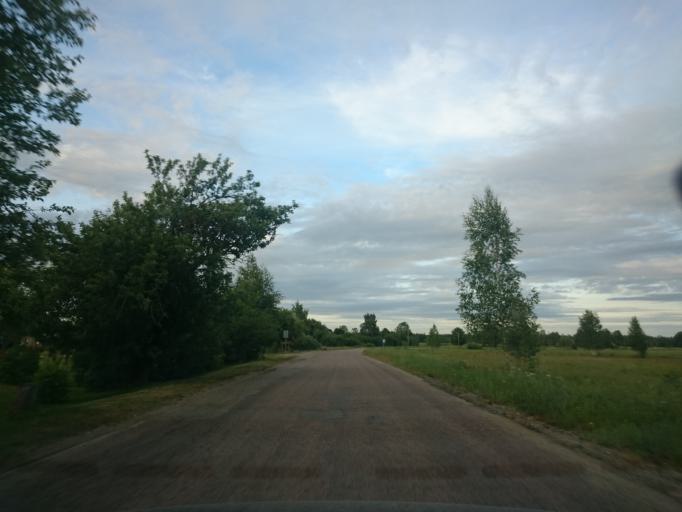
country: LV
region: Ropazu
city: Ropazi
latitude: 56.9679
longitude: 24.6720
